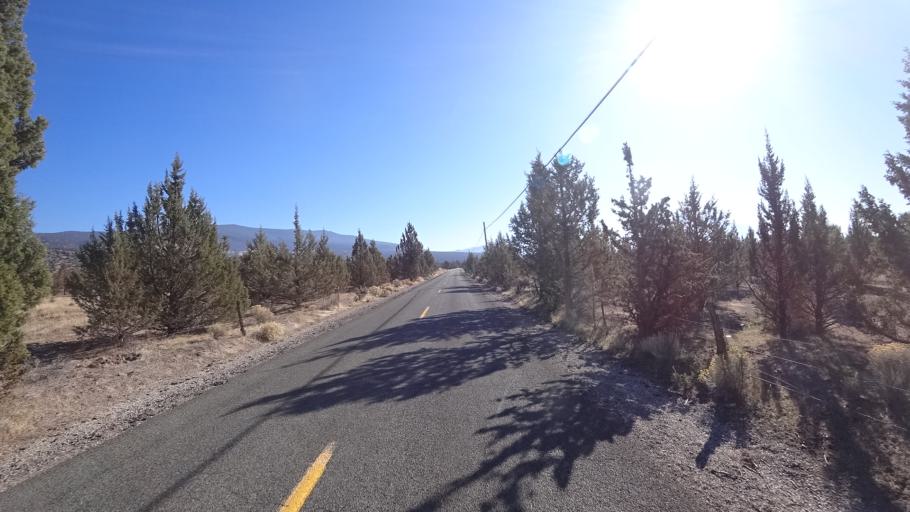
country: US
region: California
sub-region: Siskiyou County
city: Montague
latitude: 41.6438
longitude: -122.3518
